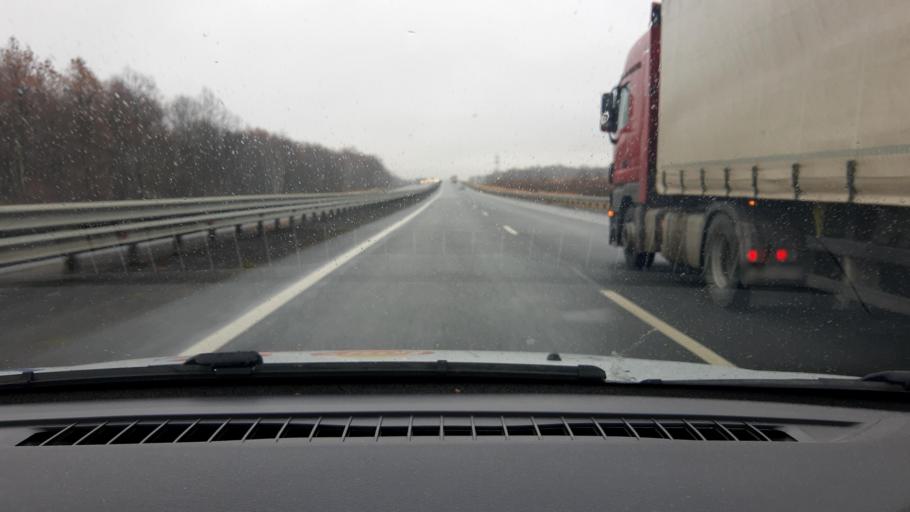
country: RU
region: Nizjnij Novgorod
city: Burevestnik
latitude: 56.1399
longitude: 43.7632
